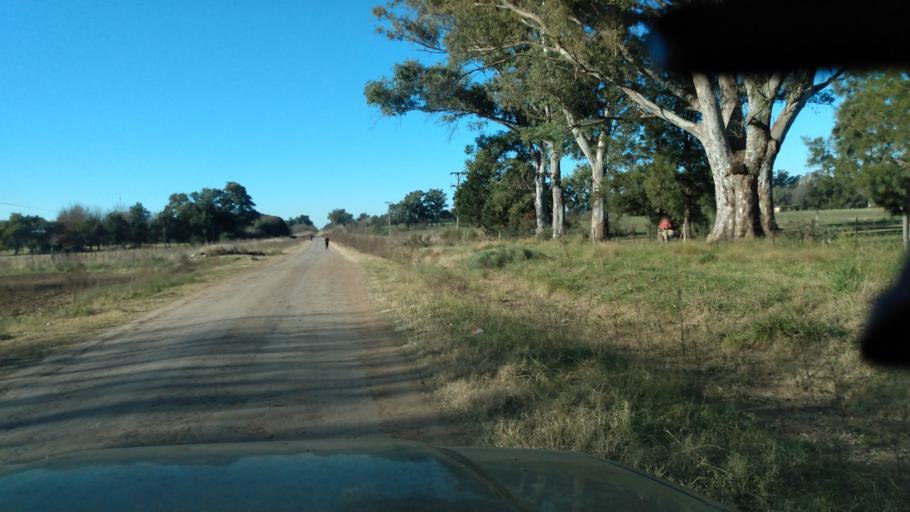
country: AR
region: Buenos Aires
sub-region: Partido de Lujan
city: Lujan
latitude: -34.5652
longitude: -59.1699
